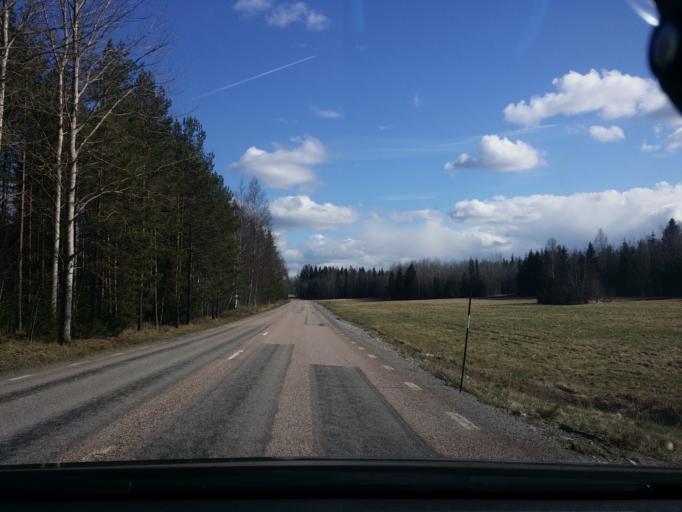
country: SE
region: Vaestmanland
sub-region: Sala Kommun
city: Sala
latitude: 59.9791
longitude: 16.4917
